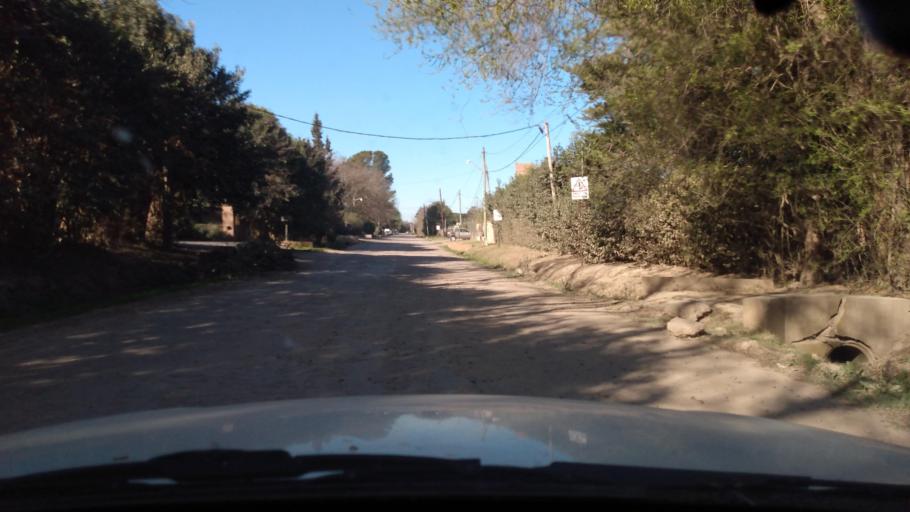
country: AR
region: Buenos Aires
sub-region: Partido de Mercedes
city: Mercedes
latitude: -34.6489
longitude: -59.4051
